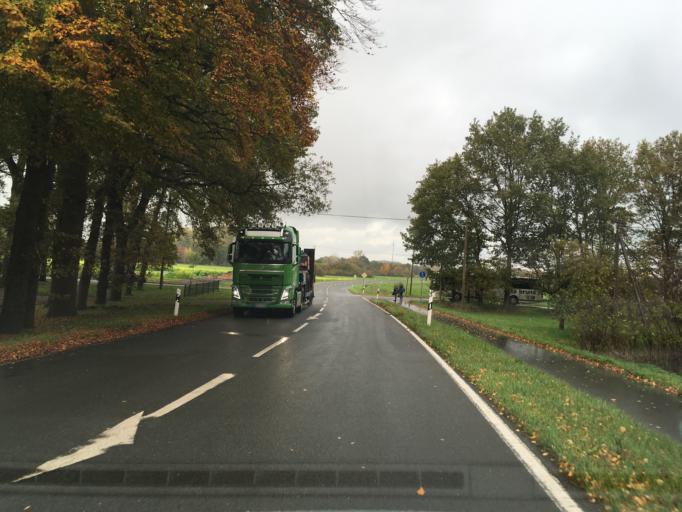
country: DE
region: North Rhine-Westphalia
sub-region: Regierungsbezirk Munster
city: Velen
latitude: 51.8533
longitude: 7.0310
